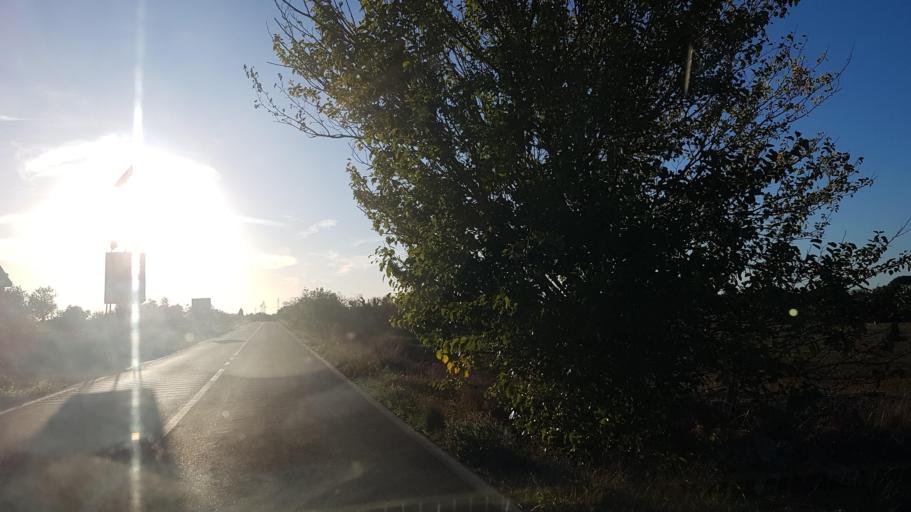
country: IT
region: Apulia
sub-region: Provincia di Lecce
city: Giorgilorio
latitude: 40.4189
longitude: 18.2118
